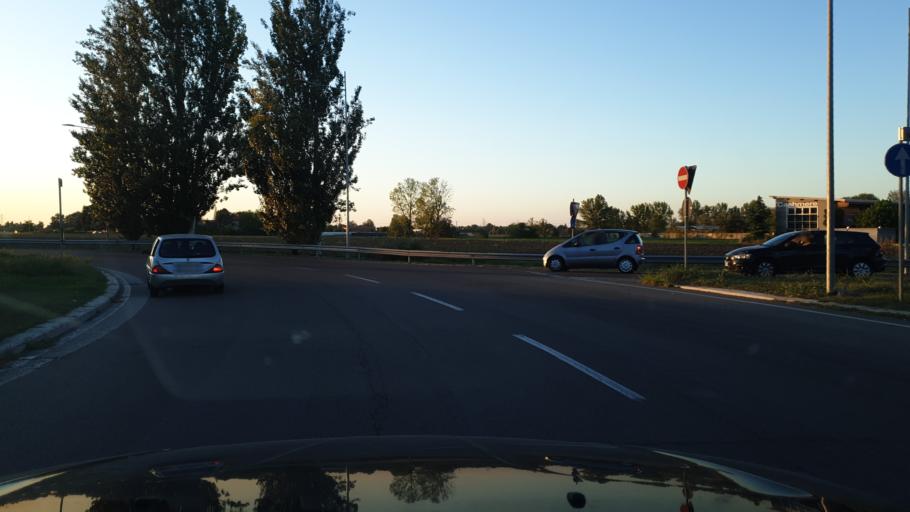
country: IT
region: Emilia-Romagna
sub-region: Provincia di Bologna
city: Quarto Inferiore
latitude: 44.5166
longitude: 11.3939
